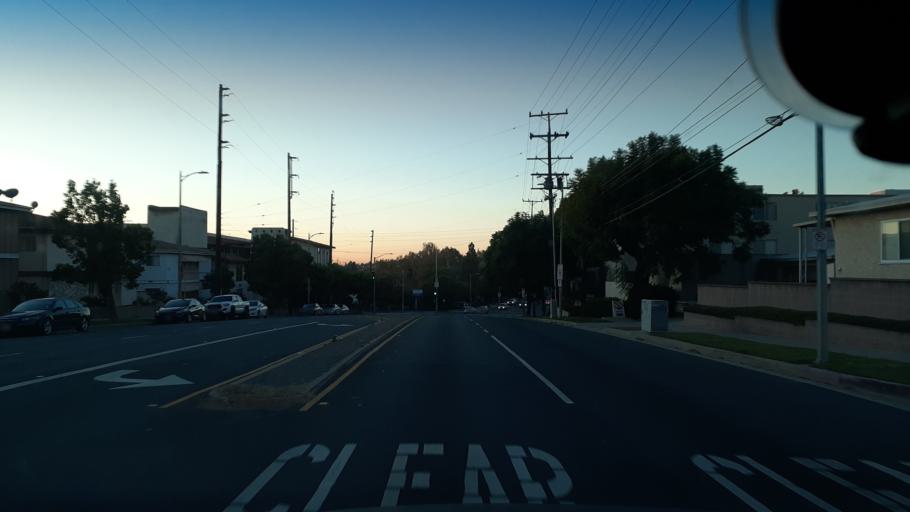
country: US
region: California
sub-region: Los Angeles County
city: San Pedro
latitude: 33.7446
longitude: -118.3097
